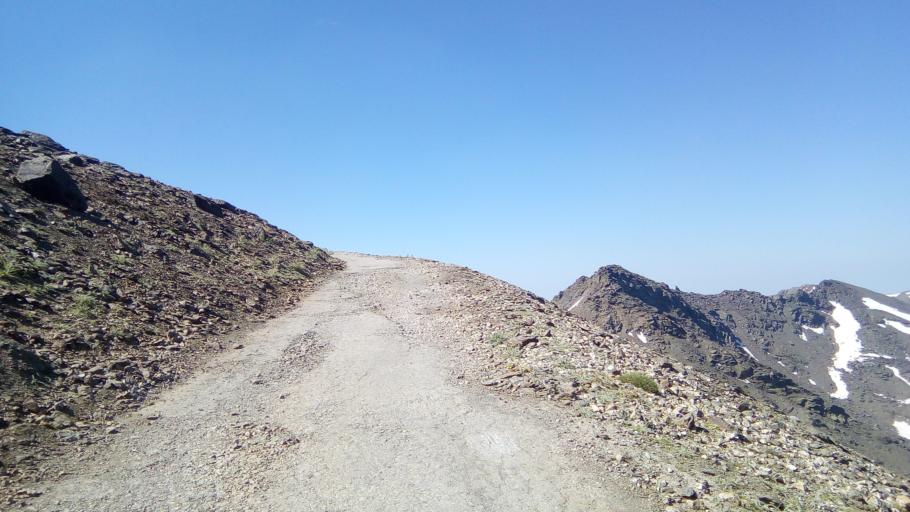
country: ES
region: Andalusia
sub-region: Provincia de Granada
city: Capileira
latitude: 37.0528
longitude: -3.3713
